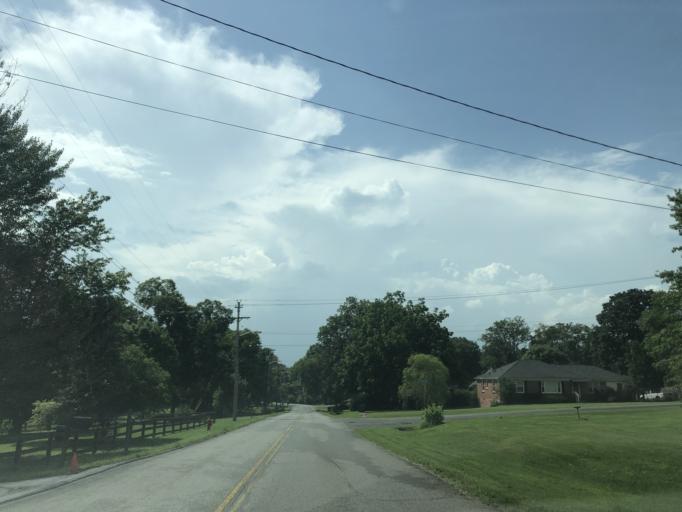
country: US
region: Tennessee
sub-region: Davidson County
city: Lakewood
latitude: 36.1764
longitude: -86.6751
